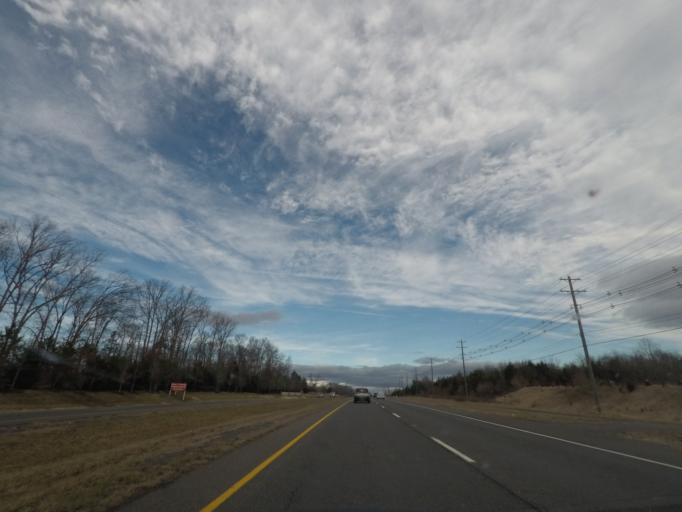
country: US
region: Virginia
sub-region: Prince William County
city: Bull Run Mountain Estates
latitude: 38.8612
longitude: -77.6369
